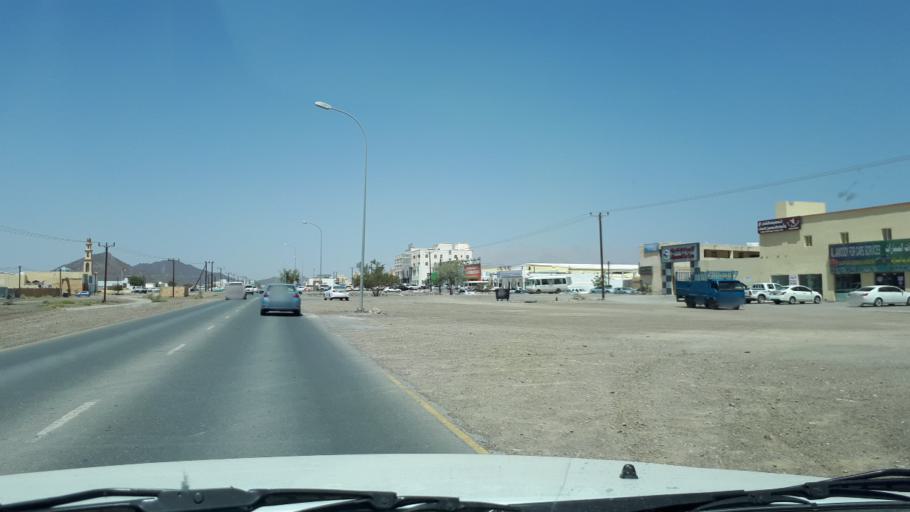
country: OM
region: Muhafazat ad Dakhiliyah
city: Bahla'
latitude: 22.9473
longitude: 57.2774
